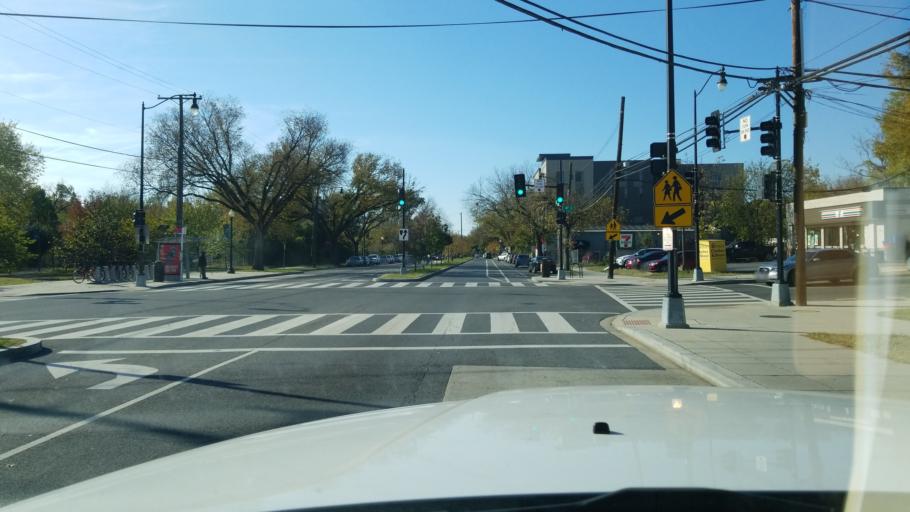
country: US
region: Maryland
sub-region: Prince George's County
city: Fairmount Heights
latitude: 38.8986
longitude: -76.9313
